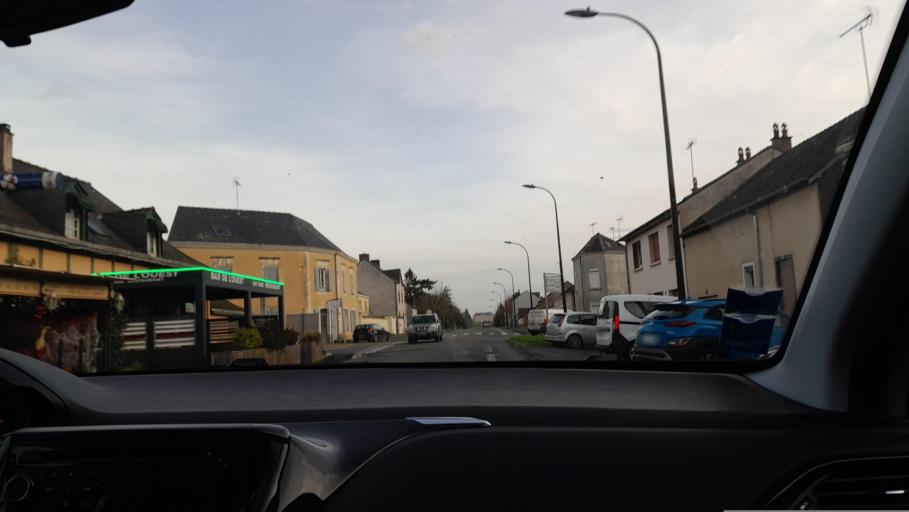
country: FR
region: Pays de la Loire
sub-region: Departement de la Mayenne
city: Craon
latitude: 47.8460
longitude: -0.9628
